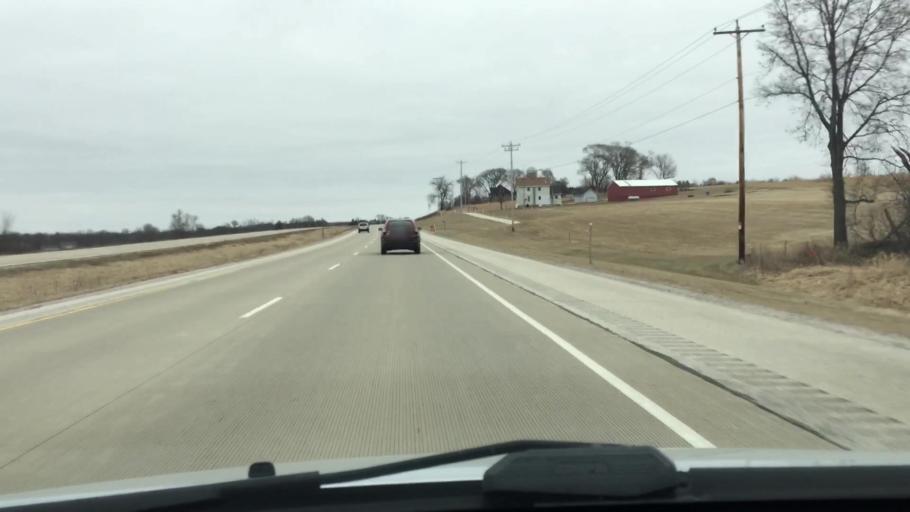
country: US
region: Wisconsin
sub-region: Jefferson County
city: Johnson Creek
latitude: 43.1104
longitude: -88.7519
